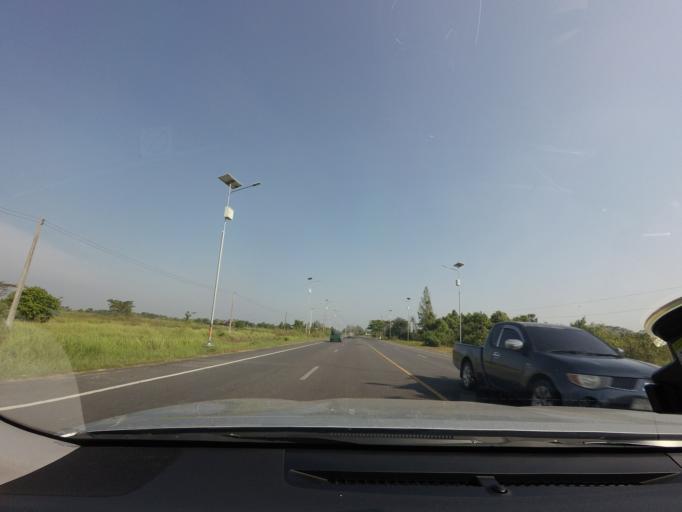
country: TH
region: Nakhon Si Thammarat
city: Nakhon Si Thammarat
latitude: 8.4977
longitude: 99.9722
